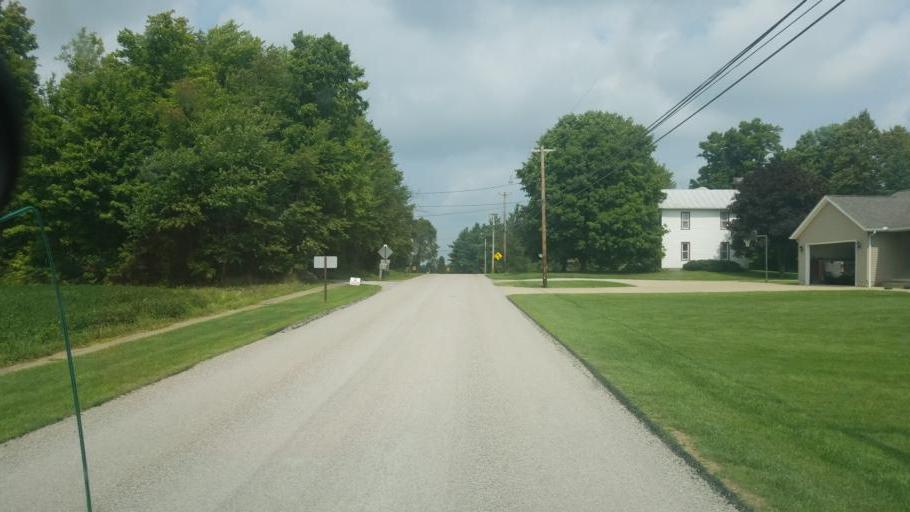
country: US
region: Ohio
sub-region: Huron County
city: Greenwich
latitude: 41.0420
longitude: -82.5160
